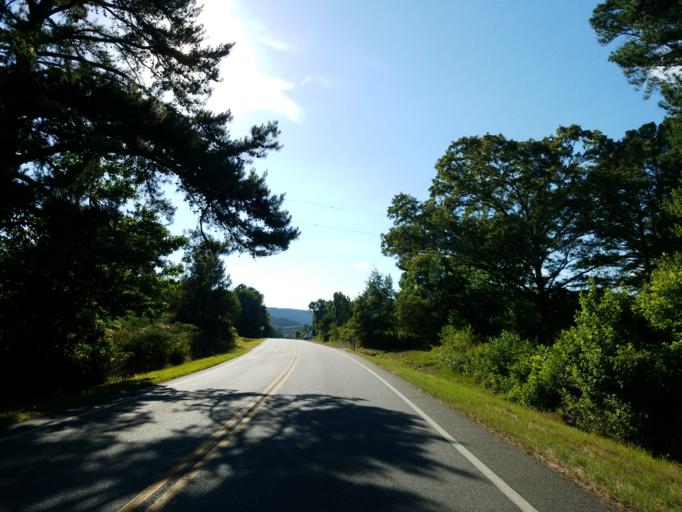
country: US
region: Georgia
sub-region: Gordon County
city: Calhoun
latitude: 34.5941
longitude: -85.0245
